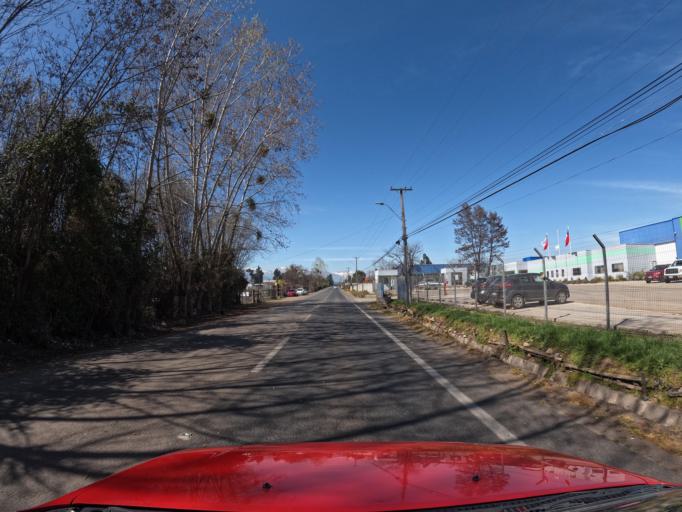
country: CL
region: Maule
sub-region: Provincia de Curico
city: Teno
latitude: -34.9644
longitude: -71.0584
